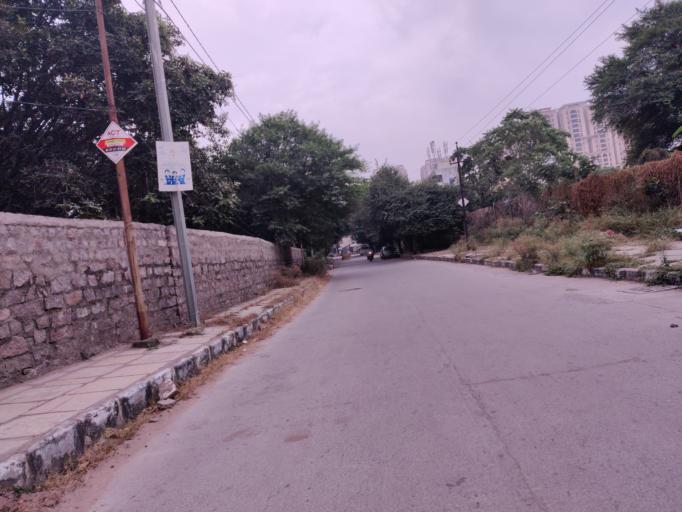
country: IN
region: Telangana
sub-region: Hyderabad
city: Hyderabad
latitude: 17.4071
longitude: 78.3996
